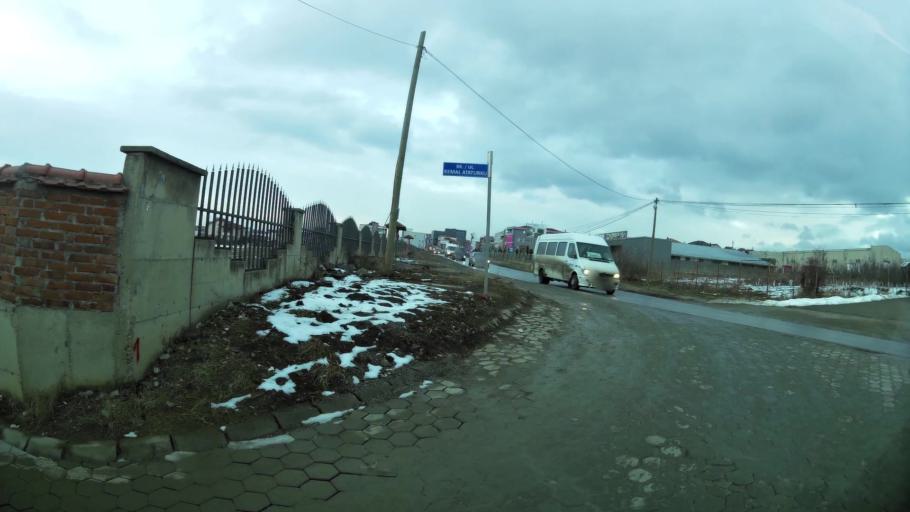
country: XK
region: Pristina
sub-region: Komuna e Prishtines
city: Pristina
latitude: 42.6223
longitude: 21.1597
